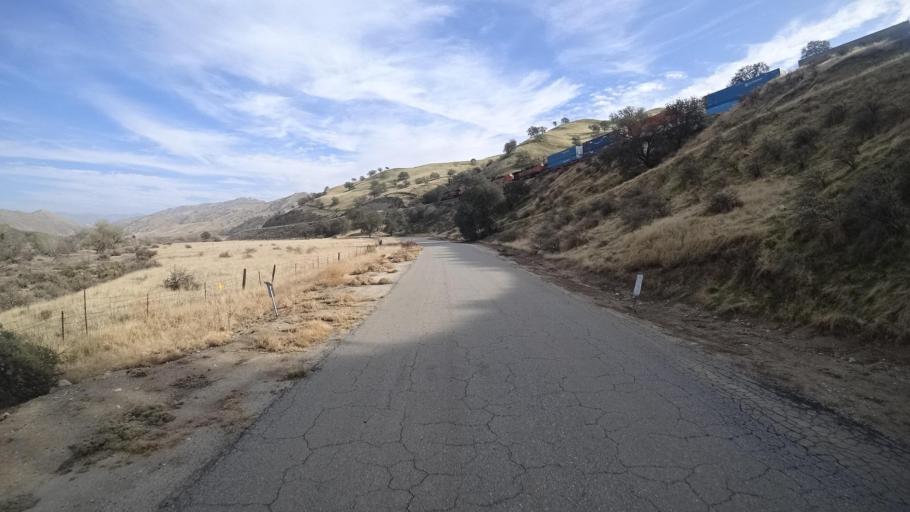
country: US
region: California
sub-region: Kern County
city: Bear Valley Springs
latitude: 35.2877
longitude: -118.6355
